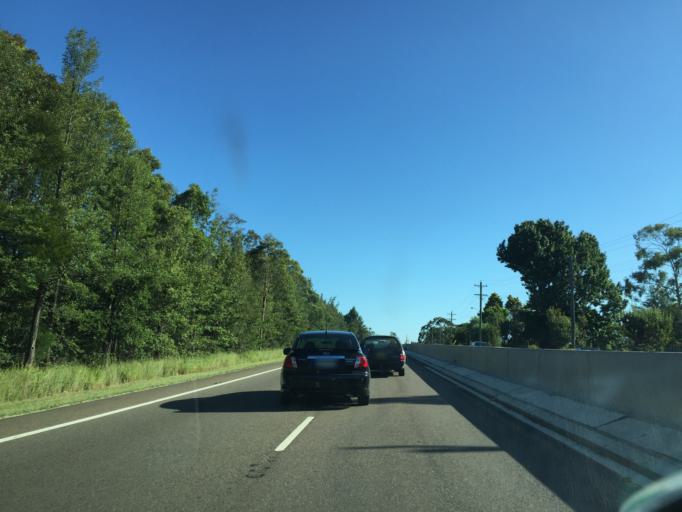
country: AU
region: New South Wales
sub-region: Blue Mountains Municipality
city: Blaxland
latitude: -33.7292
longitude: 150.6051
